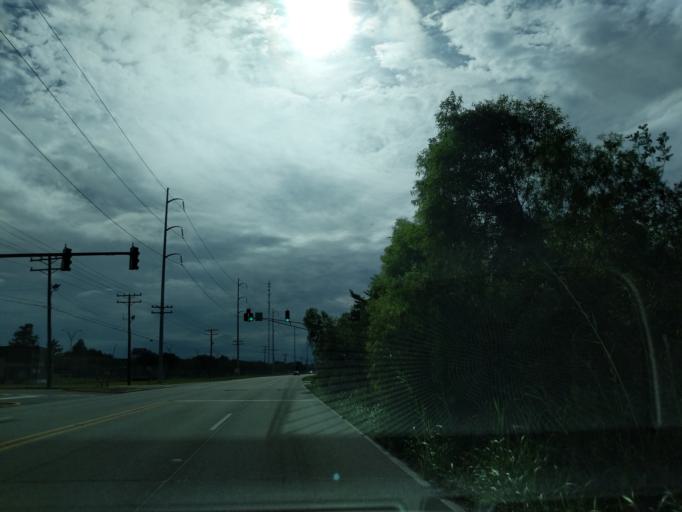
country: US
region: Louisiana
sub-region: Saint Bernard Parish
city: Chalmette
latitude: 30.0241
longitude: -89.9201
